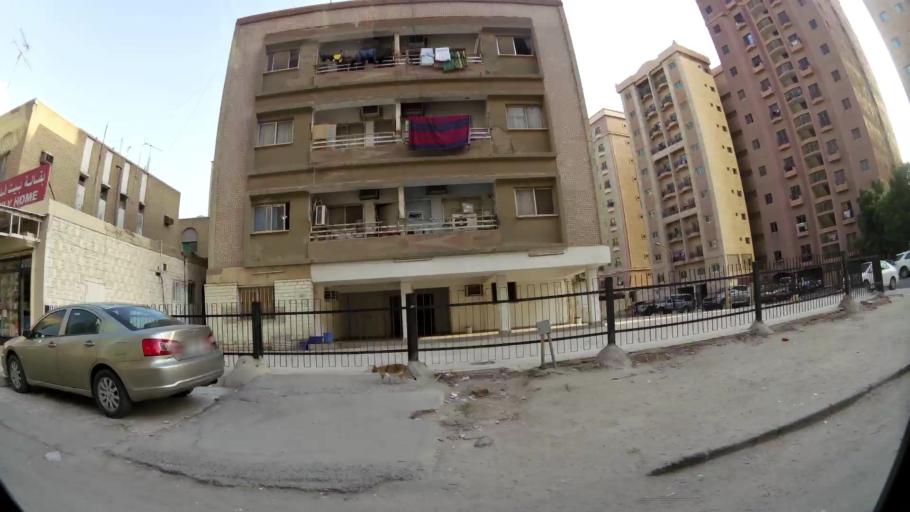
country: KW
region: Muhafazat Hawalli
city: As Salimiyah
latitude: 29.3310
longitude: 48.0598
